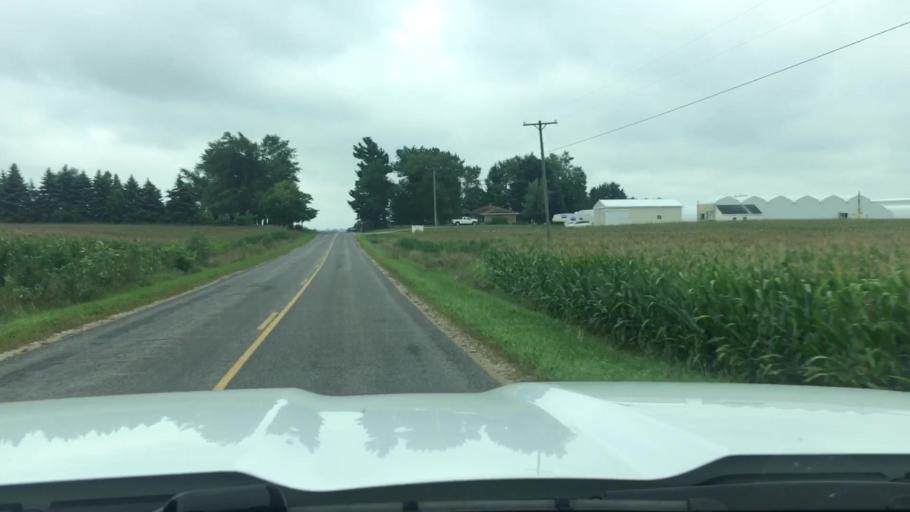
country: US
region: Michigan
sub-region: Ottawa County
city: Hudsonville
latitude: 42.7878
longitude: -85.8617
